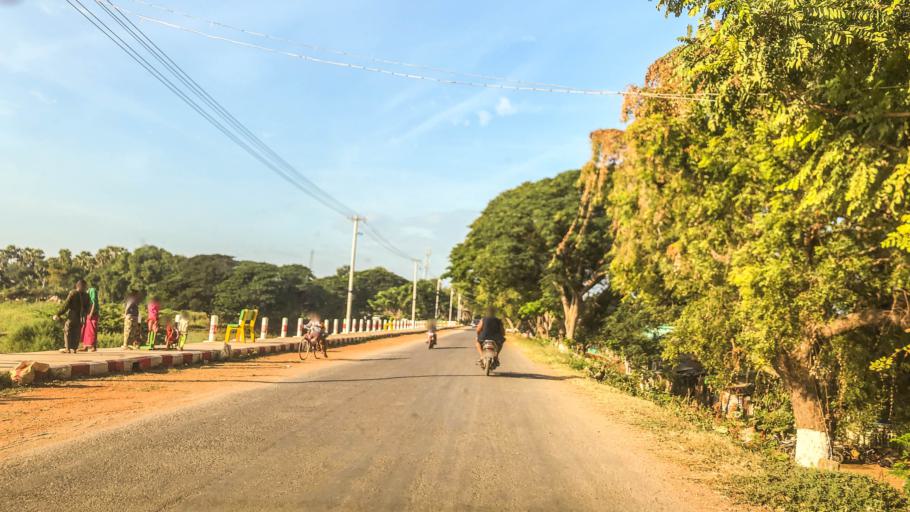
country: MM
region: Magway
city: Magway
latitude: 19.9678
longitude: 95.0426
